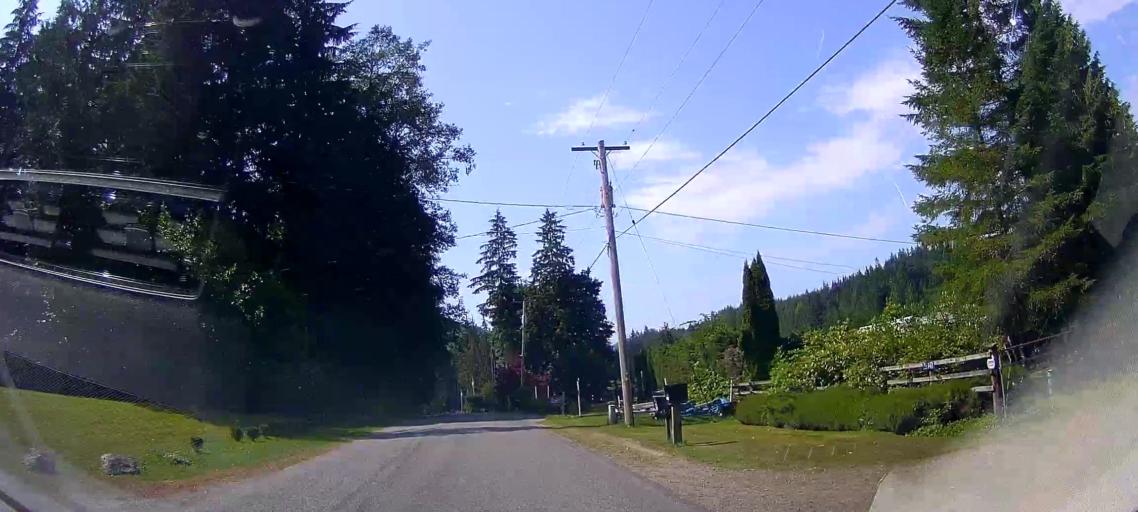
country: US
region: Washington
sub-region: Snohomish County
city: Arlington Heights
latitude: 48.3216
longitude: -122.0342
